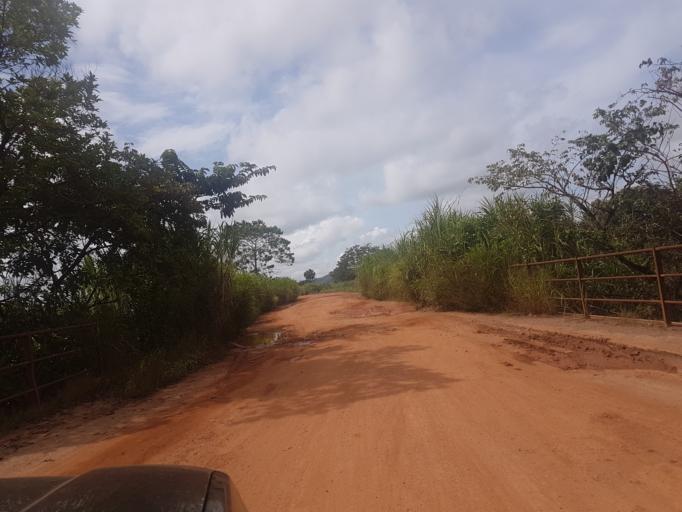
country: GN
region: Nzerekore
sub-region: Prefecture de Guekedou
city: Gueckedou
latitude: 8.6822
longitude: -10.1224
